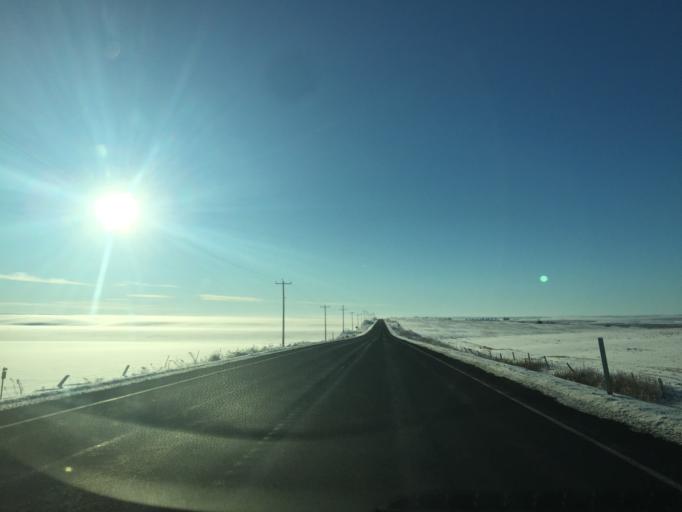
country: US
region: Washington
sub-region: Okanogan County
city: Coulee Dam
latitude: 47.7281
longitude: -118.8755
